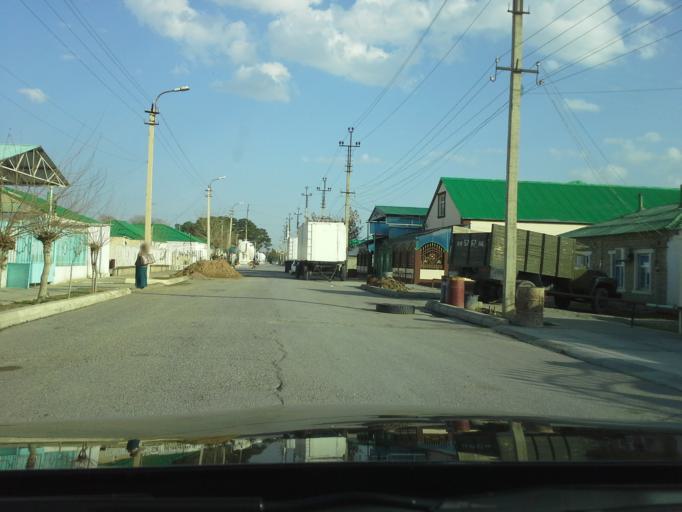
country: TM
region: Ahal
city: Abadan
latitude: 38.0258
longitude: 58.2373
